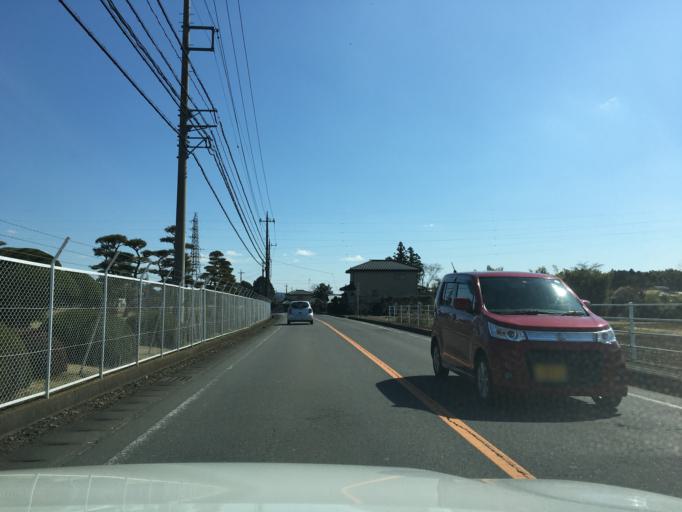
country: JP
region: Tochigi
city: Karasuyama
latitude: 36.7432
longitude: 140.1341
